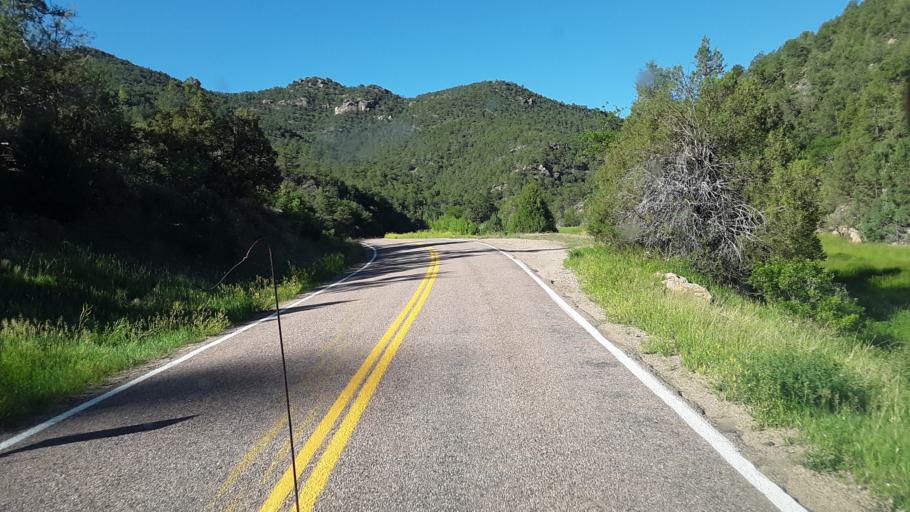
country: US
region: Colorado
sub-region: Fremont County
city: Canon City
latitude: 38.4163
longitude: -105.4134
